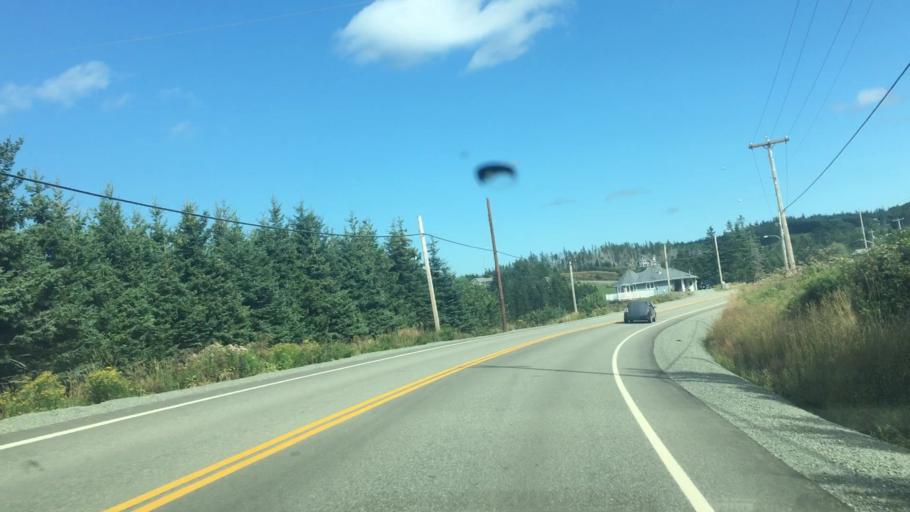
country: CA
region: Nova Scotia
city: Princeville
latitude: 45.6505
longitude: -60.8493
